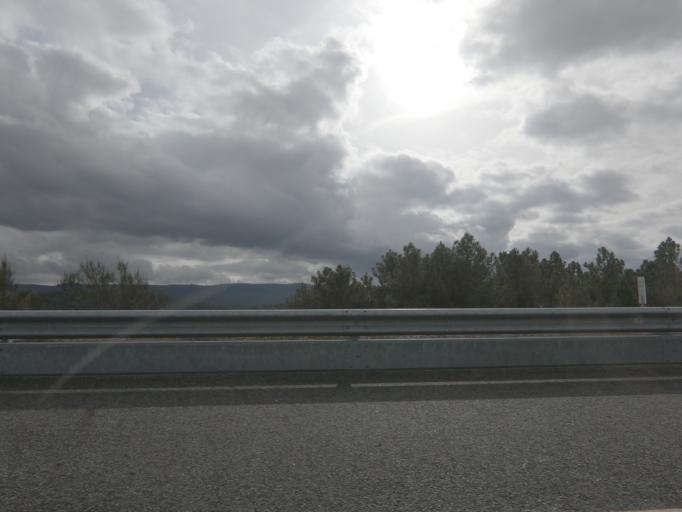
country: PT
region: Vila Real
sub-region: Chaves
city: Chaves
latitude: 41.7979
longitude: -7.4195
